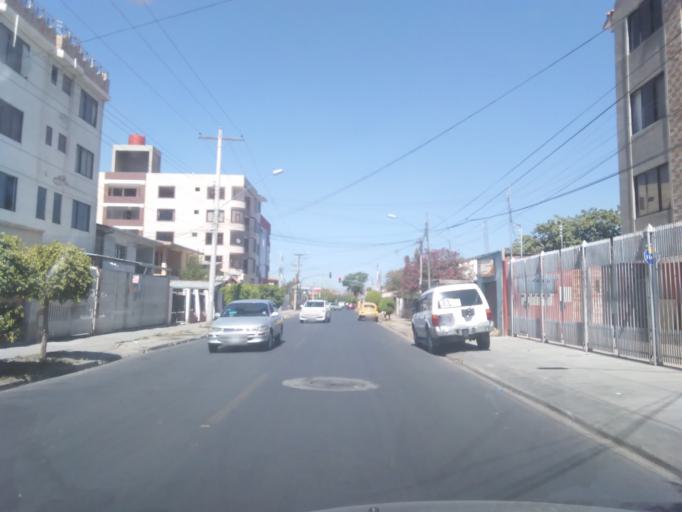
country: BO
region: Cochabamba
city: Cochabamba
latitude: -17.3954
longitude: -66.1412
